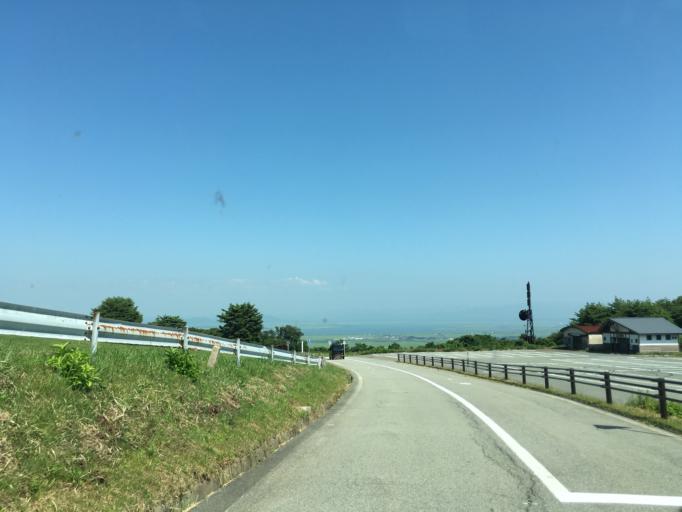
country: JP
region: Akita
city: Tenno
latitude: 39.9273
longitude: 139.8761
